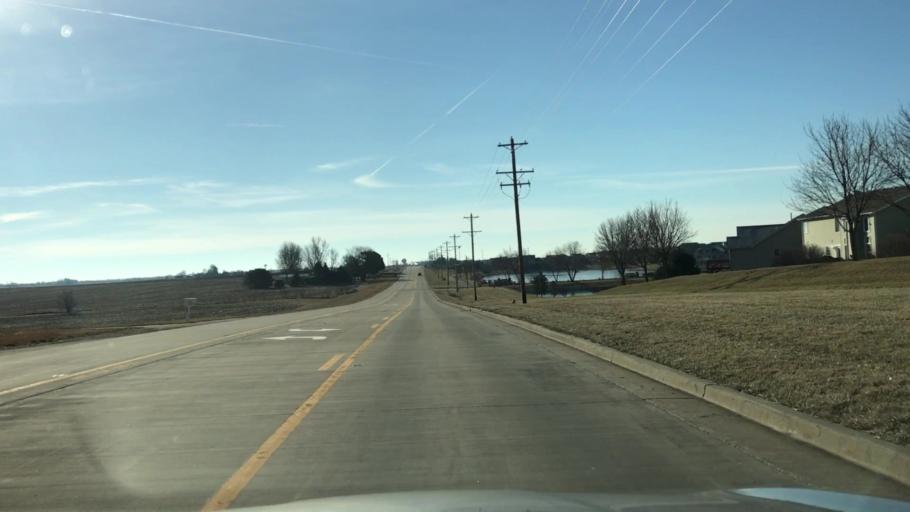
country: US
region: Illinois
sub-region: McLean County
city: Hudson
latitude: 40.5591
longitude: -88.9446
